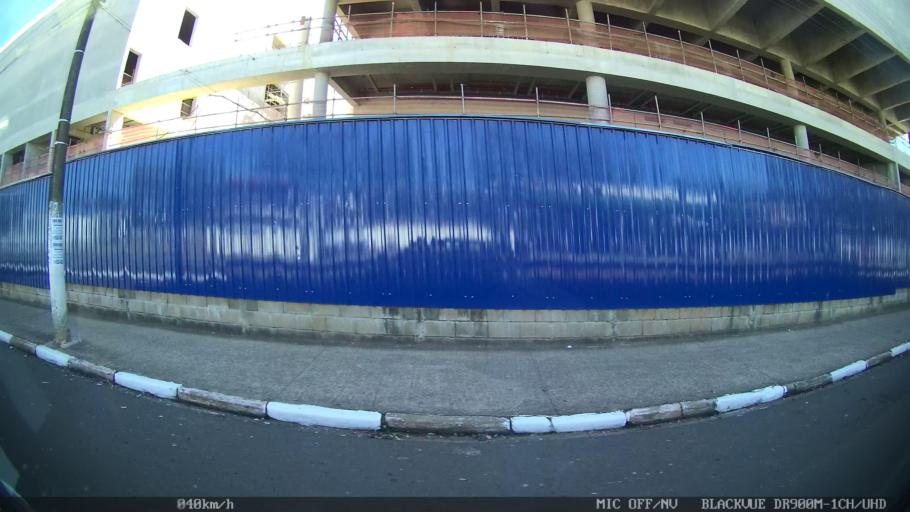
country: BR
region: Sao Paulo
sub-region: Franca
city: Franca
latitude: -20.5368
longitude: -47.3841
